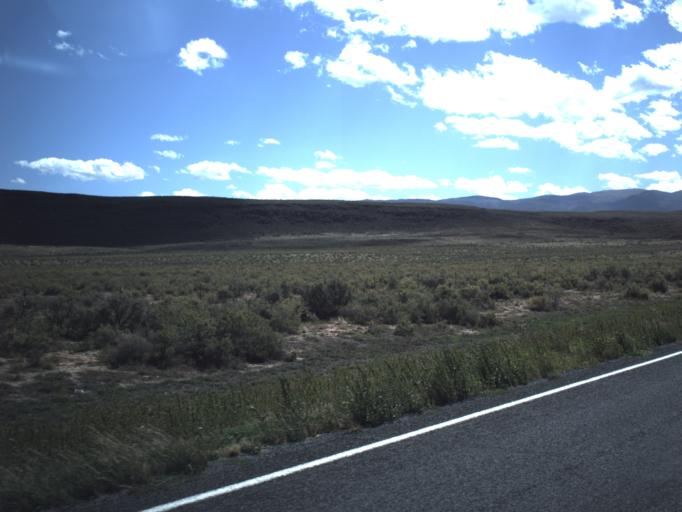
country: US
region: Utah
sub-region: Iron County
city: Enoch
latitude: 37.8649
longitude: -113.0317
